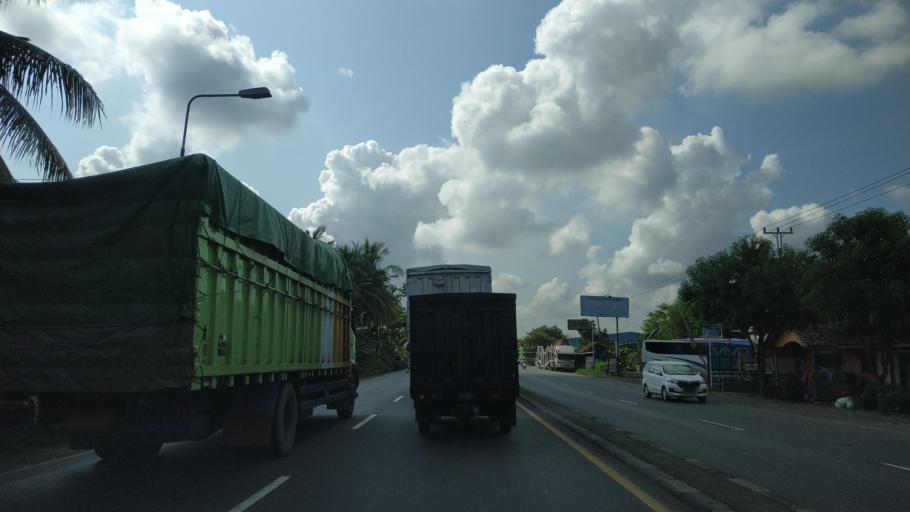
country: ID
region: Central Java
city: Comal
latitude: -6.8865
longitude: 109.5727
